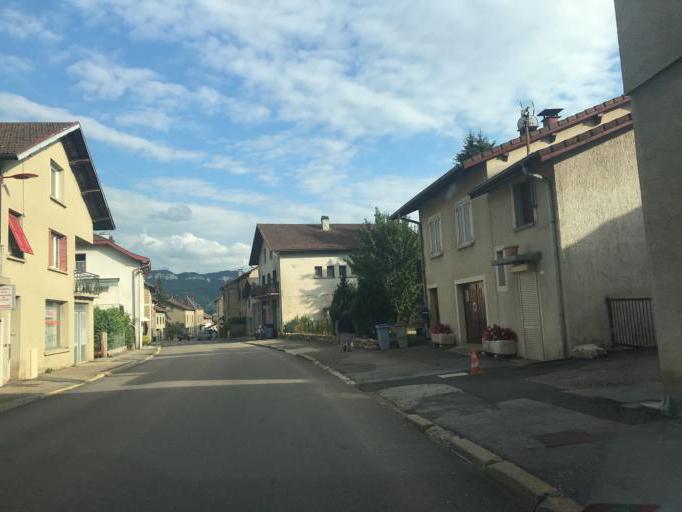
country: FR
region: Franche-Comte
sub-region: Departement du Jura
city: Saint-Lupicin
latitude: 46.3997
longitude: 5.7926
